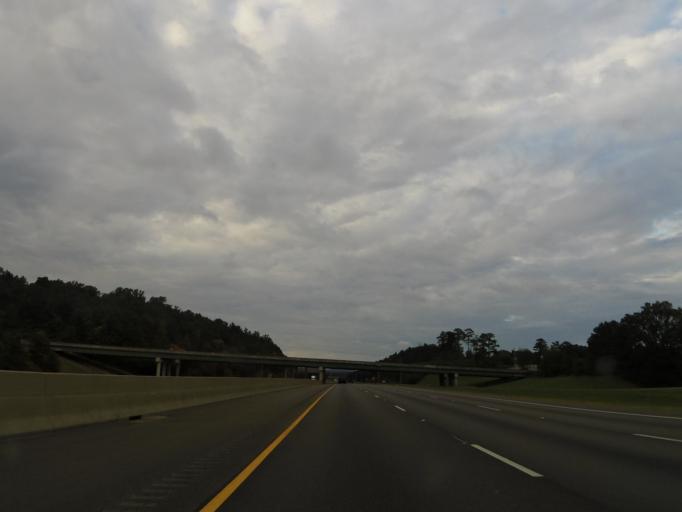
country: US
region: Alabama
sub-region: Jefferson County
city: Irondale
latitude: 33.5470
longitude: -86.6425
